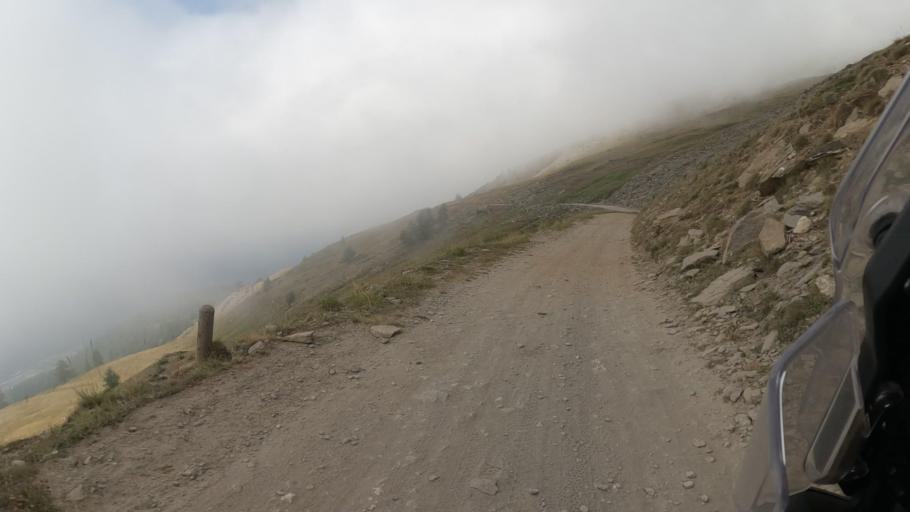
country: IT
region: Piedmont
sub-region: Provincia di Torino
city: Pragelato-Rua
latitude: 45.0380
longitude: 6.9293
